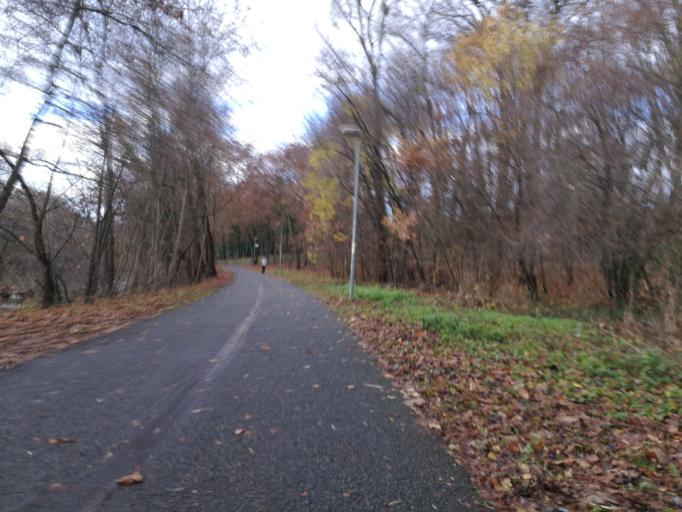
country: DE
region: Bavaria
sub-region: Regierungsbezirk Mittelfranken
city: Furth
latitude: 49.4838
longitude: 10.9921
